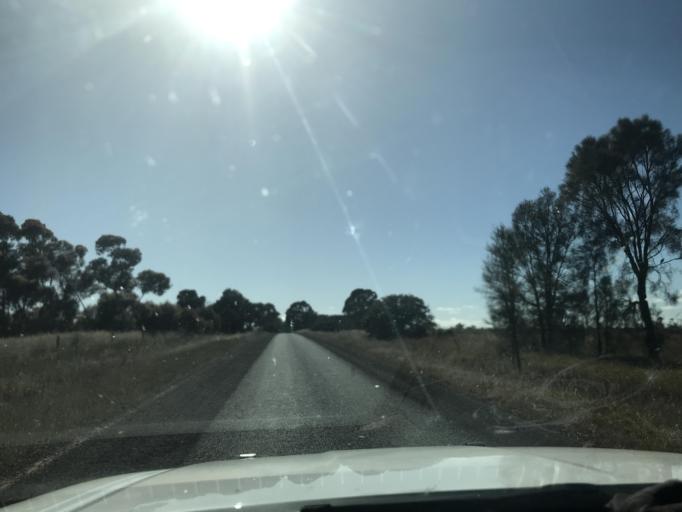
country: AU
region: Victoria
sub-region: Horsham
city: Horsham
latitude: -37.0065
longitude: 141.6354
